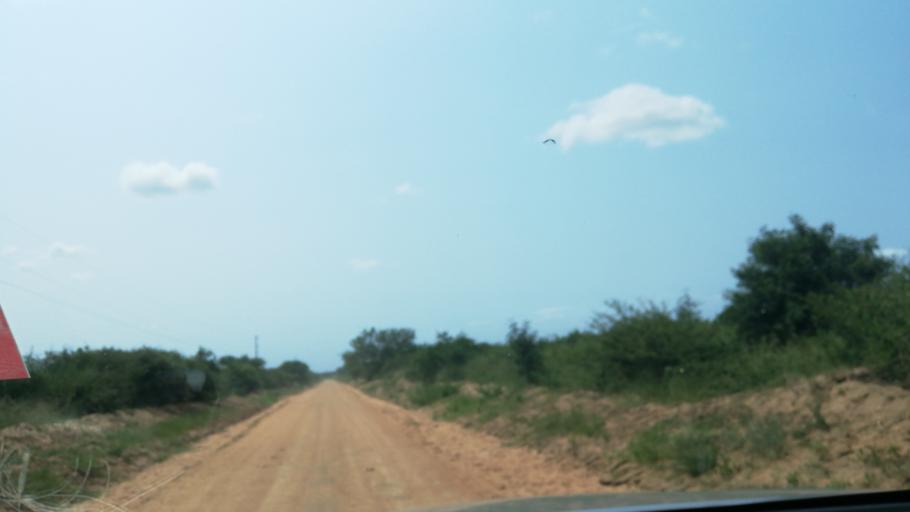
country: MZ
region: Maputo
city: Matola
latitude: -26.0916
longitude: 32.3904
